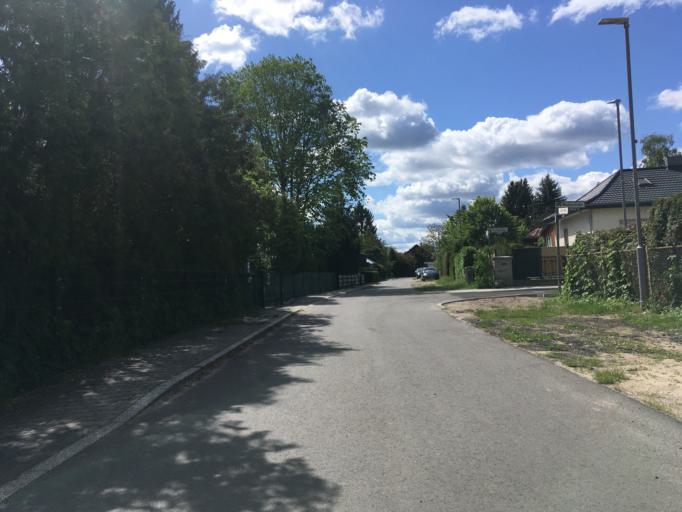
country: DE
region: Berlin
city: Bohnsdorf
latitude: 52.3981
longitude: 13.5852
